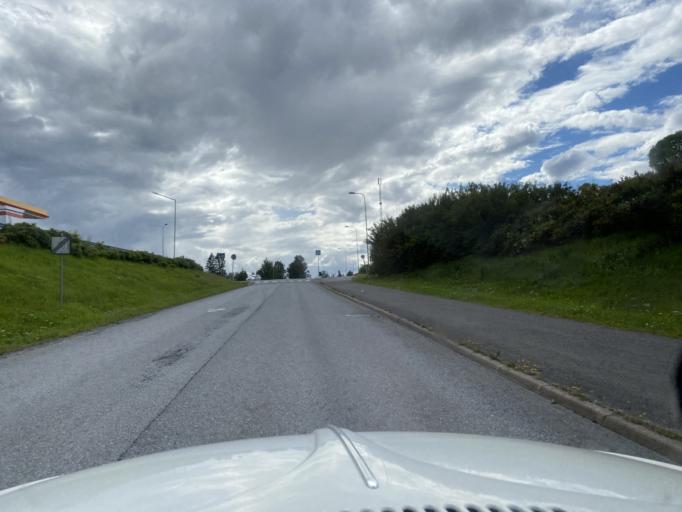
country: FI
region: Satakunta
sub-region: Pori
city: Huittinen
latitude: 61.1684
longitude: 22.6822
